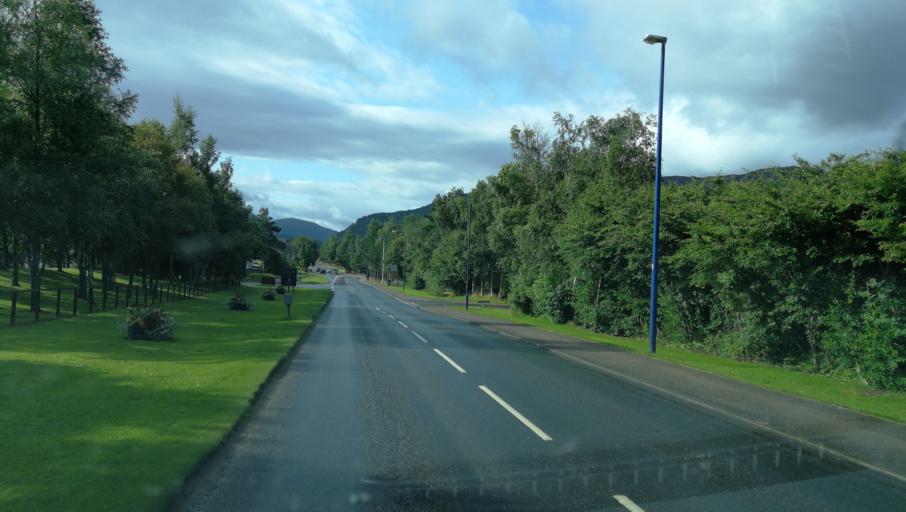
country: GB
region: Scotland
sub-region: Highland
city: Aviemore
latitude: 57.2017
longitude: -3.8277
